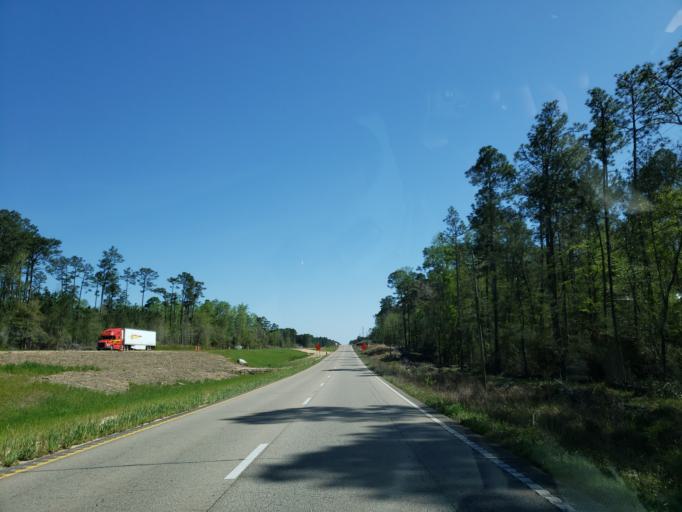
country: US
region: Mississippi
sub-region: Lamar County
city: Purvis
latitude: 31.1415
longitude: -89.2326
